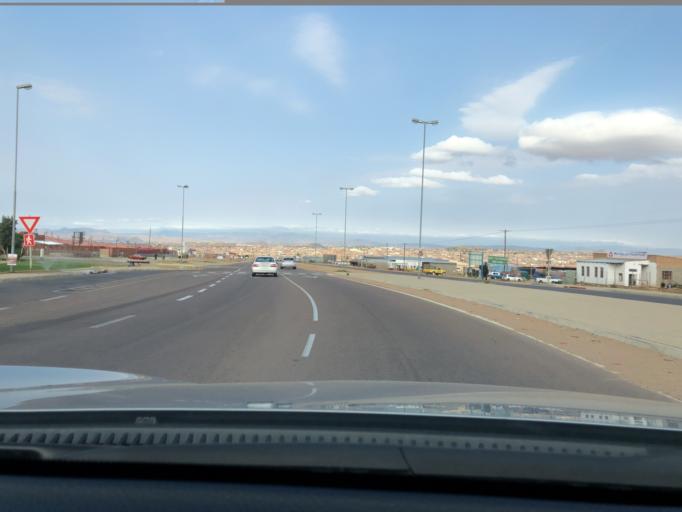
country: ZA
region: Limpopo
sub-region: Capricorn District Municipality
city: Mankoeng
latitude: -23.8892
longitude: 29.6696
